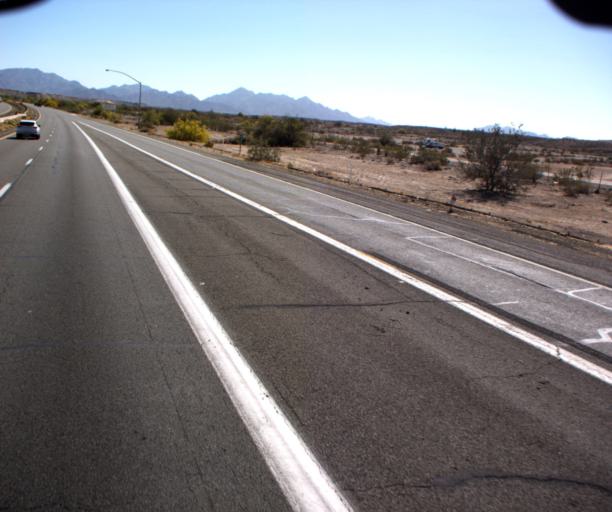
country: US
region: Arizona
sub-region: La Paz County
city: Ehrenberg
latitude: 33.6023
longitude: -114.5153
